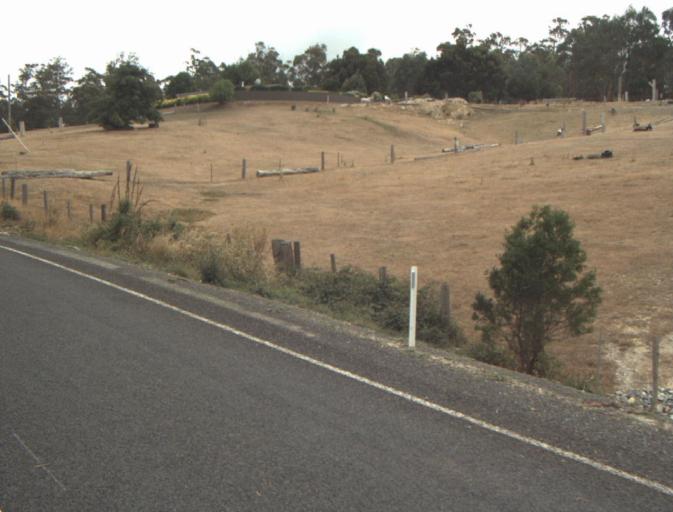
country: AU
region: Tasmania
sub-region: Dorset
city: Bridport
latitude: -41.1646
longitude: 147.2507
